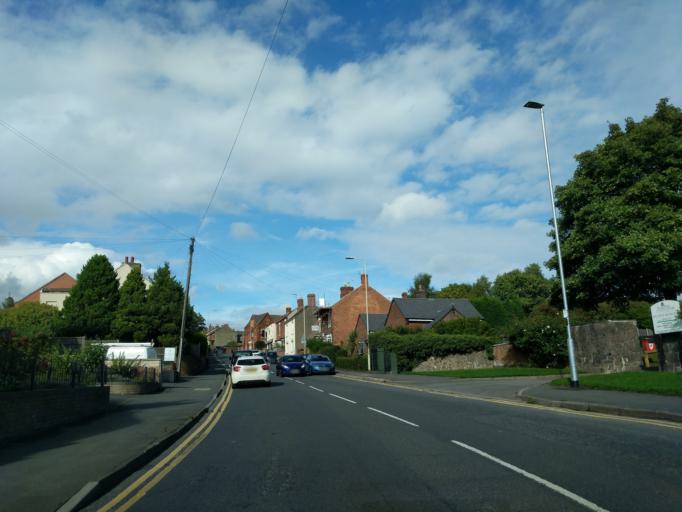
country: GB
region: England
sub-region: Leicestershire
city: Coalville
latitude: 52.7086
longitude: -1.3726
